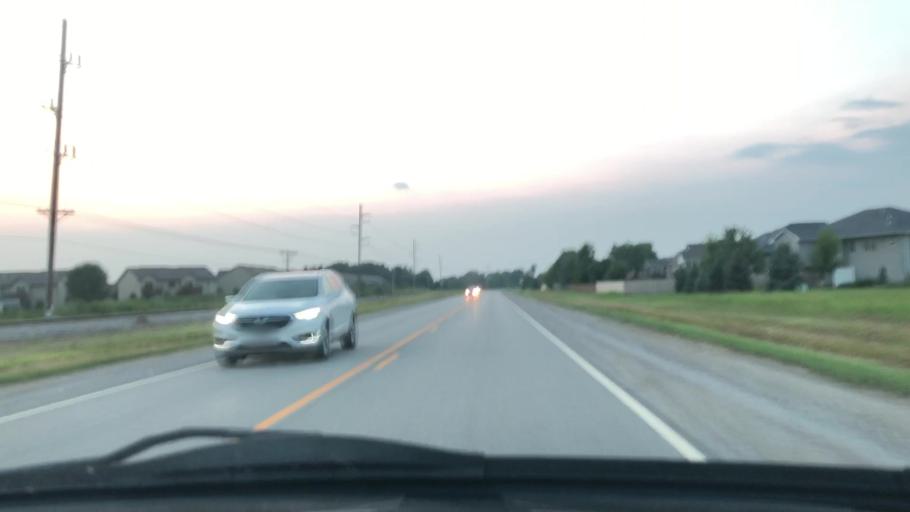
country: US
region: Iowa
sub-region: Johnson County
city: North Liberty
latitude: 41.7628
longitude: -91.6130
